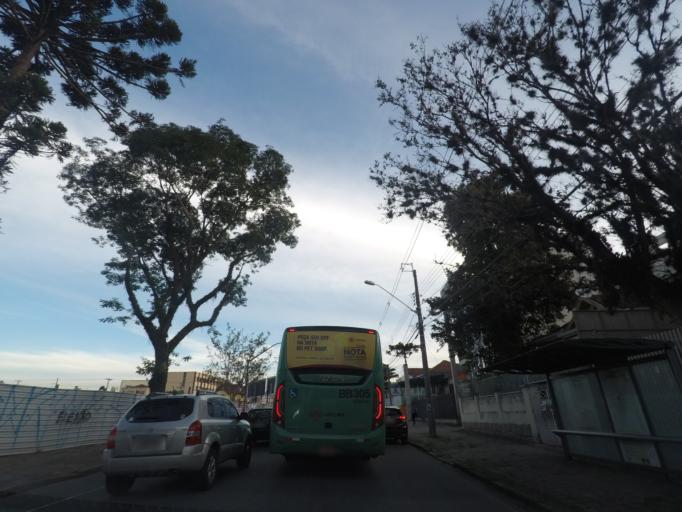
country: BR
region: Parana
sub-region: Curitiba
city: Curitiba
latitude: -25.4217
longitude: -49.2833
